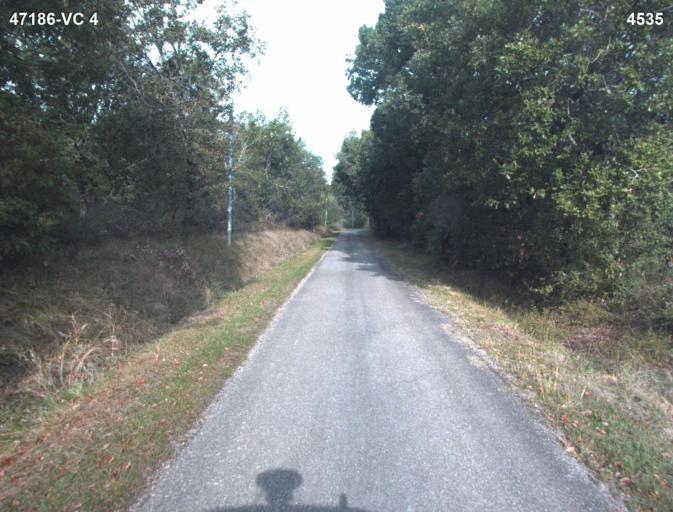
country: FR
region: Aquitaine
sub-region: Departement du Lot-et-Garonne
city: Sainte-Colombe-en-Bruilhois
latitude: 44.1933
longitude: 0.4524
